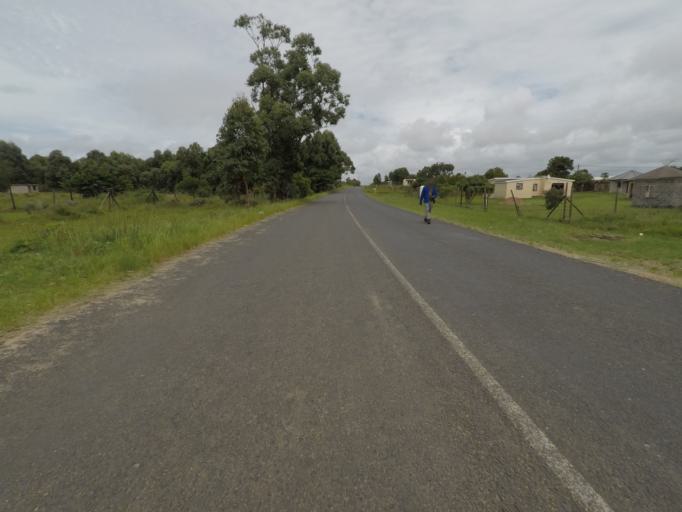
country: ZA
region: KwaZulu-Natal
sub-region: uThungulu District Municipality
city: eSikhawini
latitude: -28.9121
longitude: 31.8623
